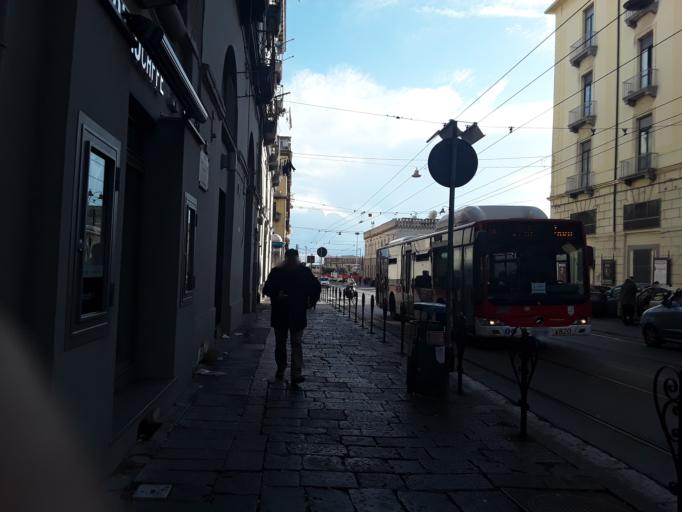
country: IT
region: Campania
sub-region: Provincia di Napoli
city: Napoli
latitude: 40.8479
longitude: 14.2689
